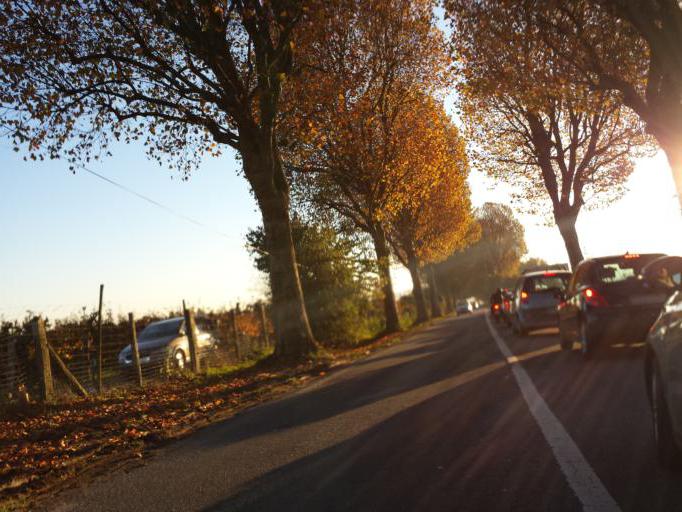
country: FR
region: Ile-de-France
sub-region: Departement du Val-d'Oise
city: Attainville
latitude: 49.0659
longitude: 2.3361
